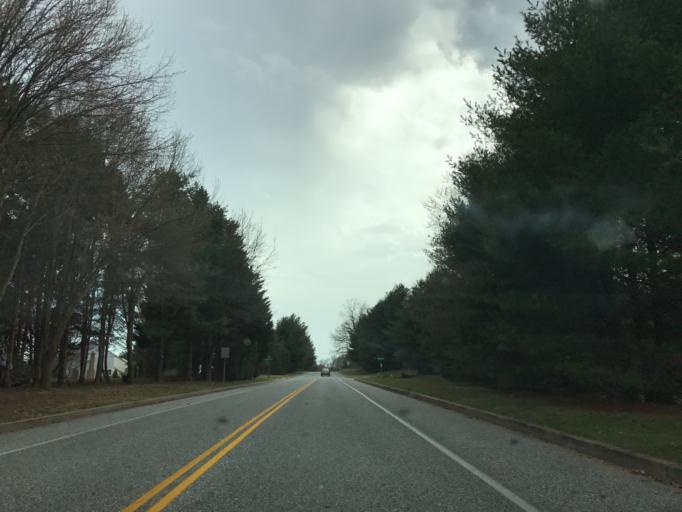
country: US
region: Maryland
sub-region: Harford County
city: South Bel Air
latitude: 39.5613
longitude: -76.3231
